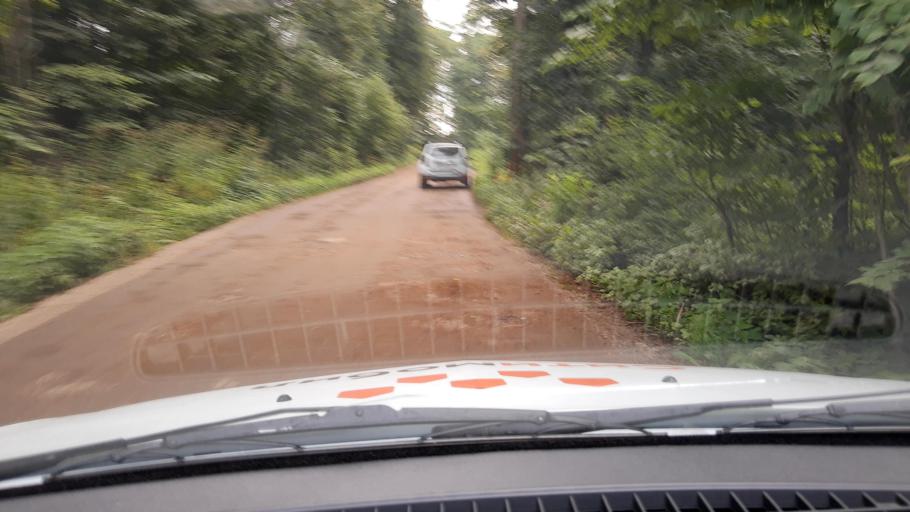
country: RU
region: Bashkortostan
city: Kabakovo
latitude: 54.7062
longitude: 56.1371
